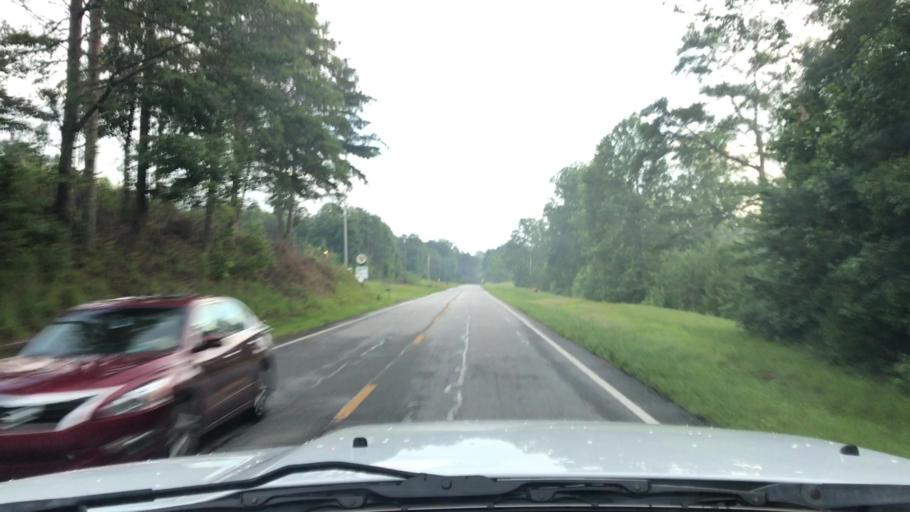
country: US
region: Georgia
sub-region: Fannin County
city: Blue Ridge
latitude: 34.9572
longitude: -84.2284
